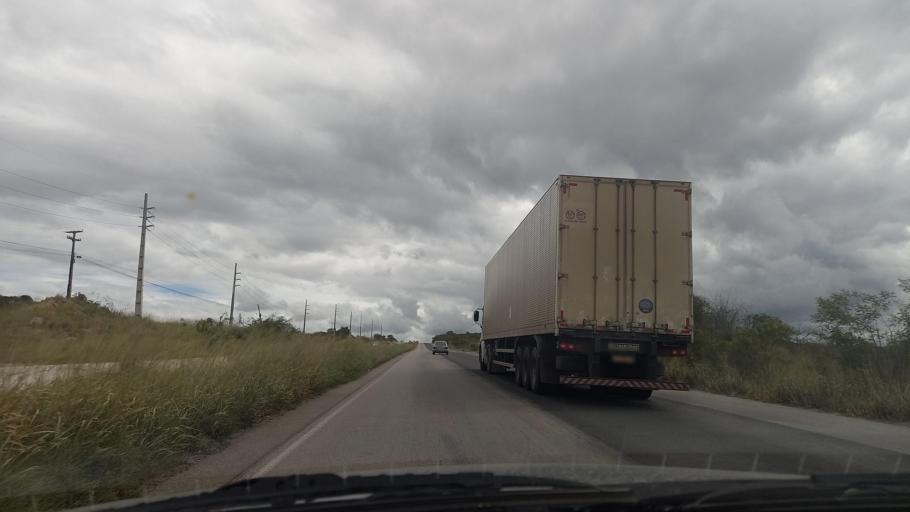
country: BR
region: Pernambuco
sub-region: Caruaru
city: Caruaru
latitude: -8.3148
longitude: -36.0466
